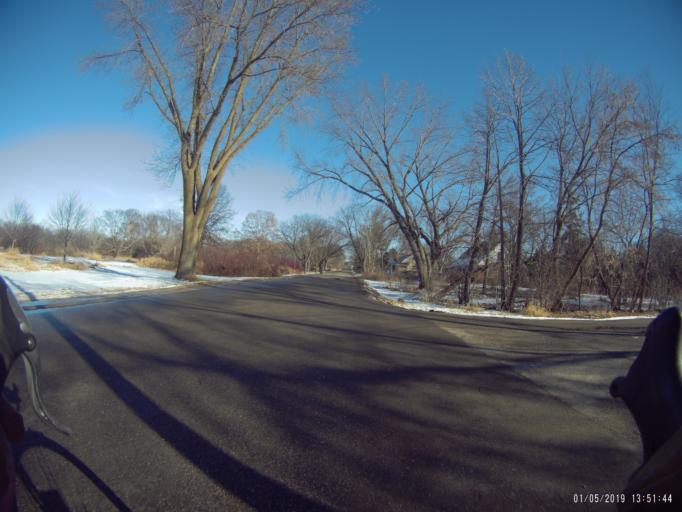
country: US
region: Wisconsin
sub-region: Dane County
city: Madison
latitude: 43.0447
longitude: -89.4093
